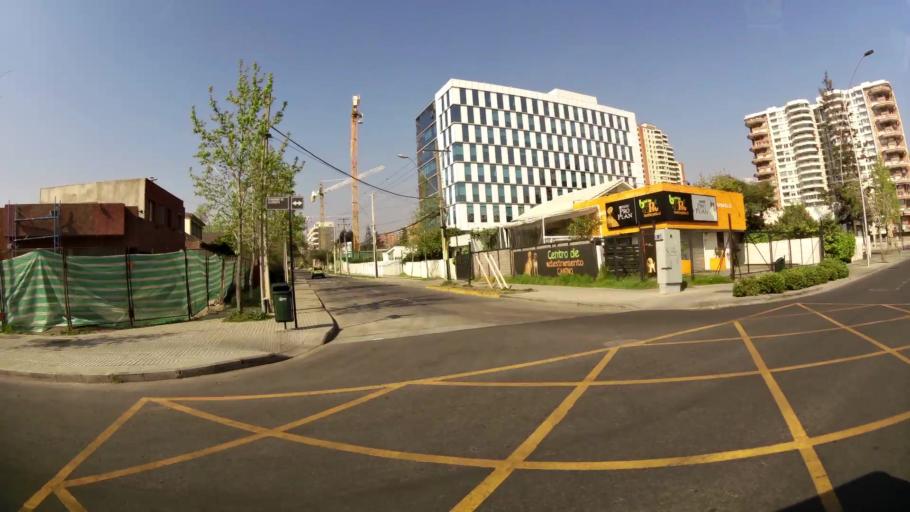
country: CL
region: Santiago Metropolitan
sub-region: Provincia de Santiago
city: Villa Presidente Frei, Nunoa, Santiago, Chile
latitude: -33.3937
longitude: -70.5620
